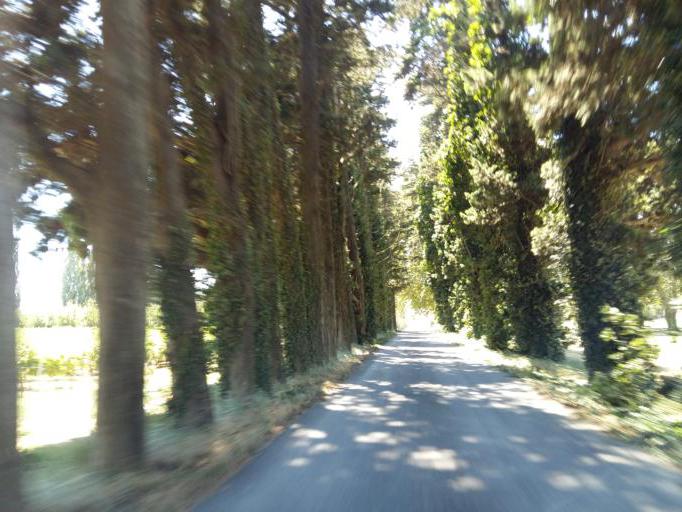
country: FR
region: Provence-Alpes-Cote d'Azur
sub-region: Departement du Vaucluse
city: Mornas
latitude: 44.1764
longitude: 4.7259
